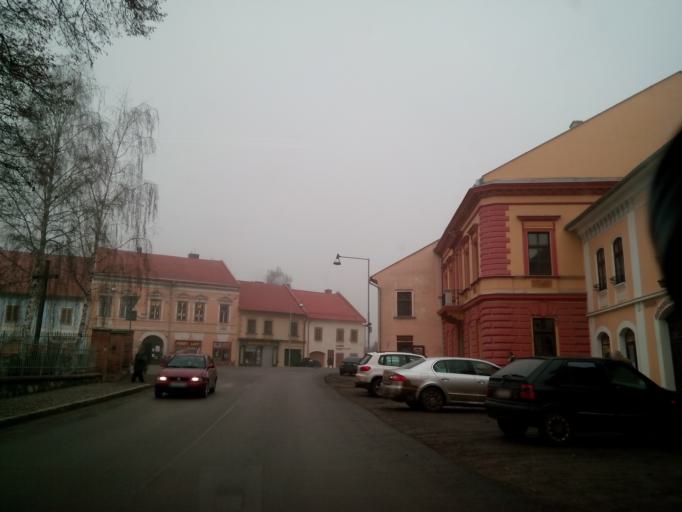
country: SK
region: Presovsky
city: Spisske Podhradie
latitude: 49.0009
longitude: 20.7525
